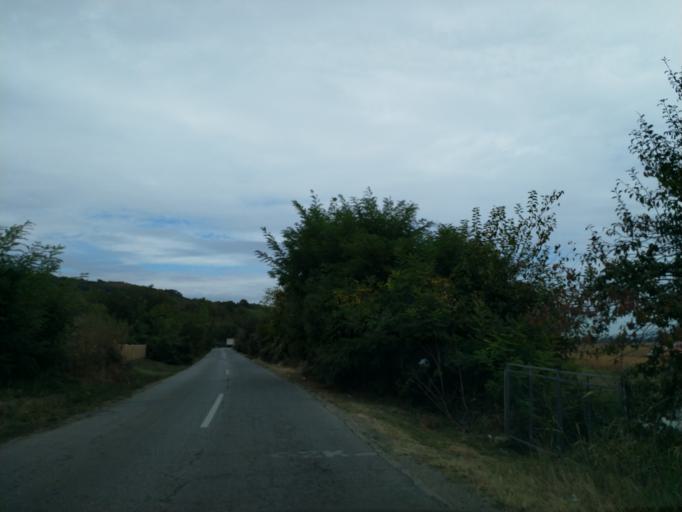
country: RS
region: Central Serbia
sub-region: Pomoravski Okrug
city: Paracin
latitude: 43.8468
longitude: 21.3224
